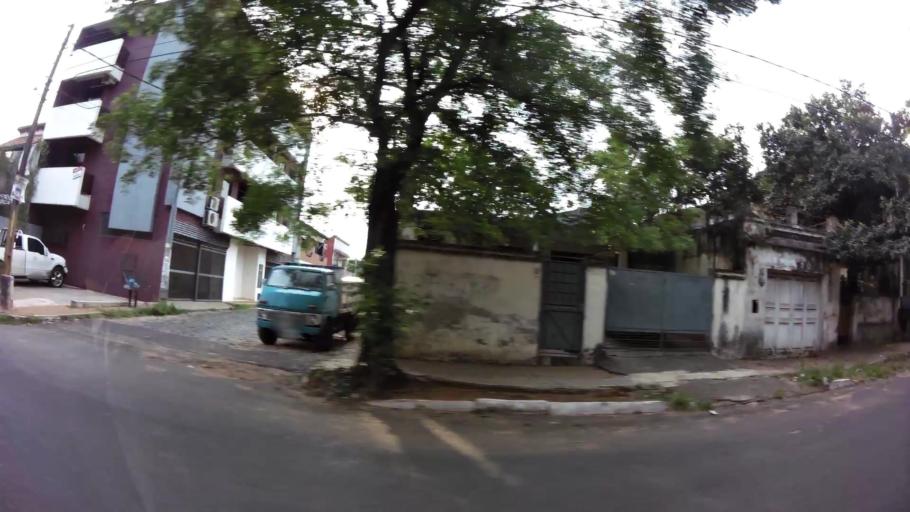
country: PY
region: Asuncion
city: Asuncion
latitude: -25.3111
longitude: -57.6105
